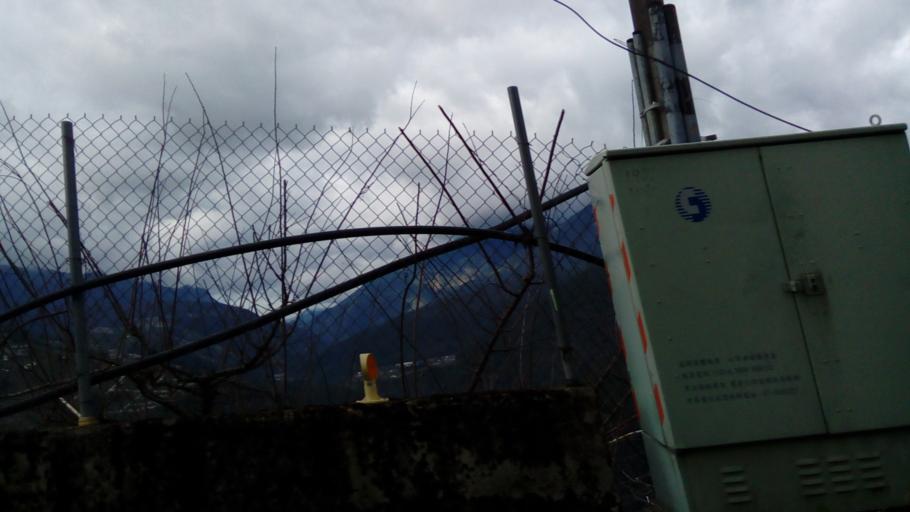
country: TW
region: Taiwan
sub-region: Nantou
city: Puli
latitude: 24.2626
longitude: 121.2615
